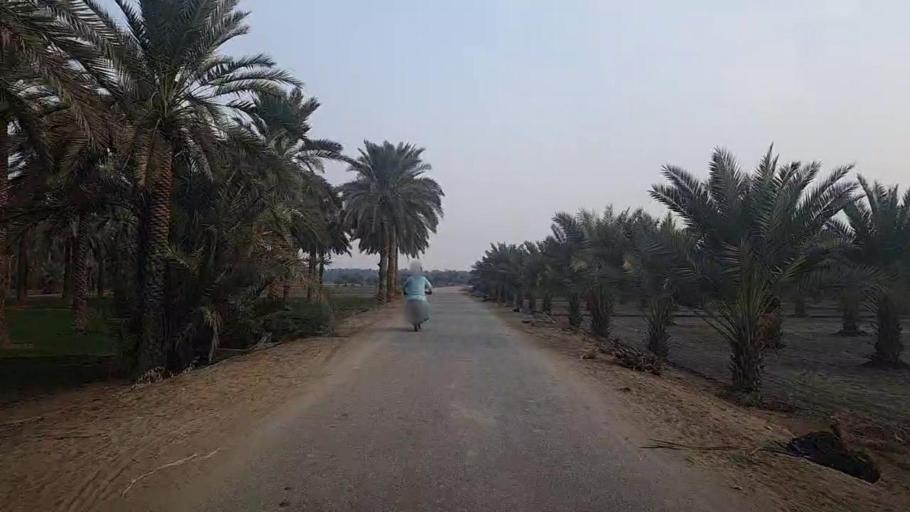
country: PK
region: Sindh
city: Kot Diji
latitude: 27.3863
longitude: 68.6589
